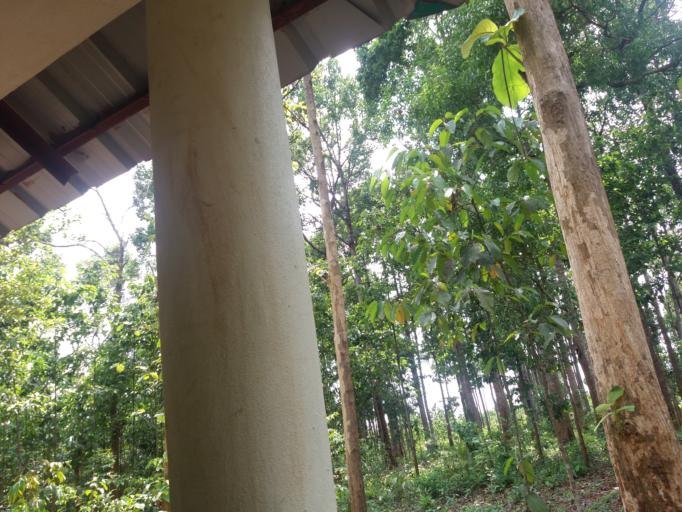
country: BD
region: Chittagong
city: Cox's Bazar
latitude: 21.7120
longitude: 92.0819
